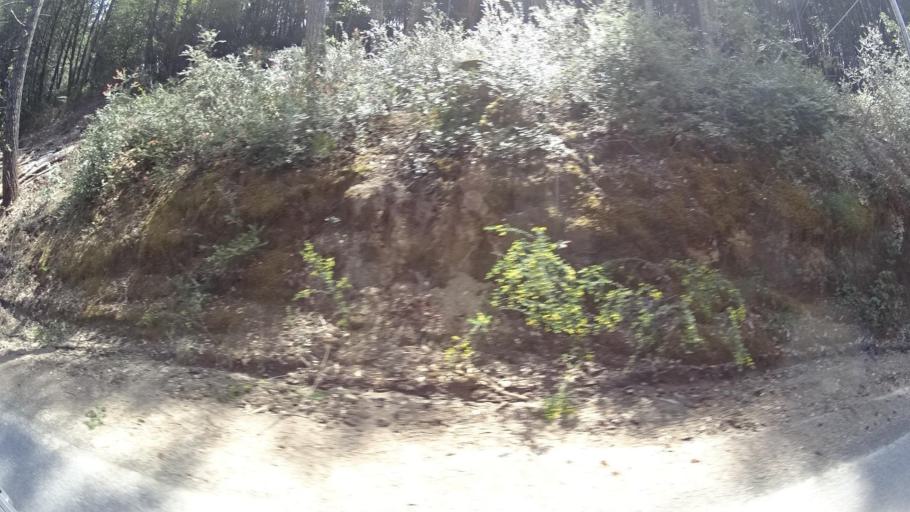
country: US
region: California
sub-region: Humboldt County
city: Redway
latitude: 40.0885
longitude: -123.9382
